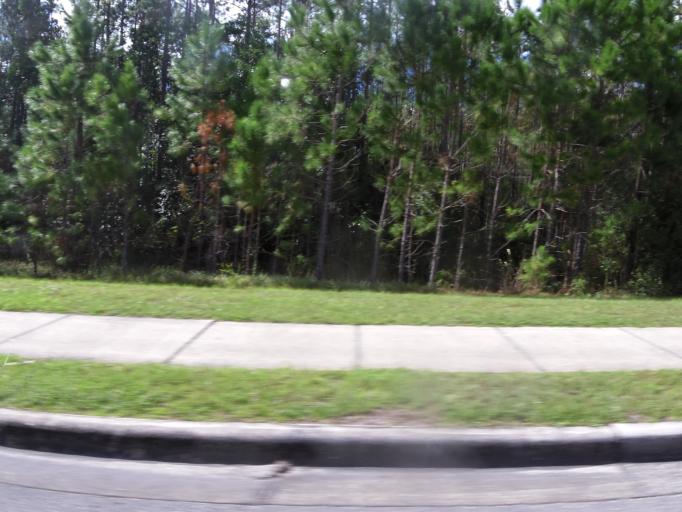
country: US
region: Florida
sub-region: Saint Johns County
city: Fruit Cove
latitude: 30.0652
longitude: -81.5318
